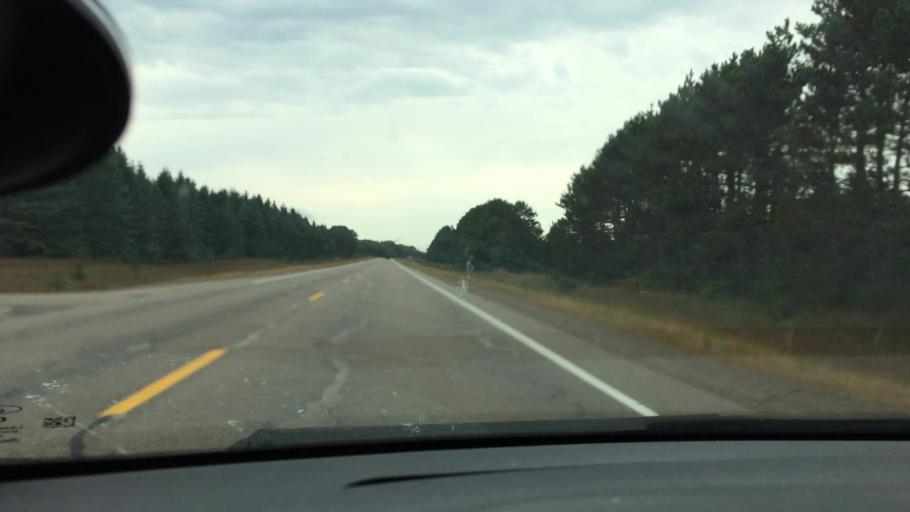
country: US
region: Wisconsin
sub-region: Eau Claire County
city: Augusta
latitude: 44.5808
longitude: -91.0697
